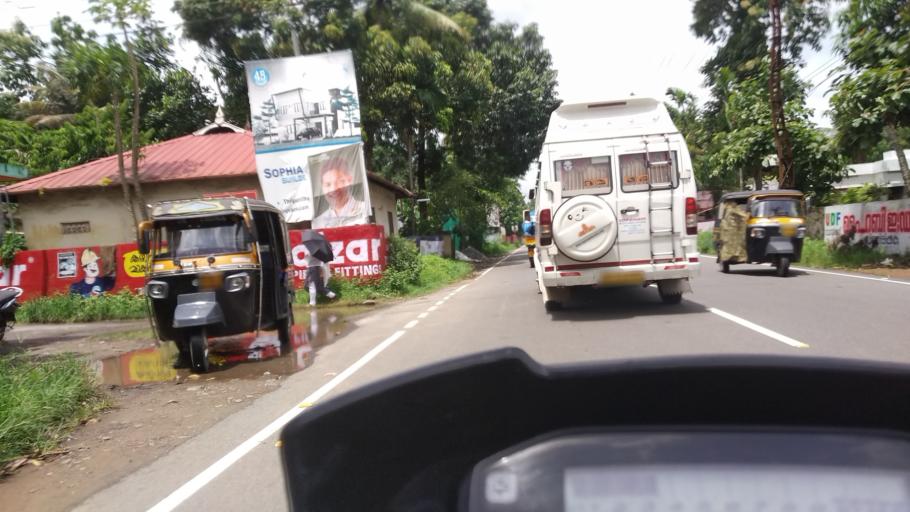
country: IN
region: Kerala
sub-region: Ernakulam
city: Elur
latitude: 10.1358
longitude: 76.2720
